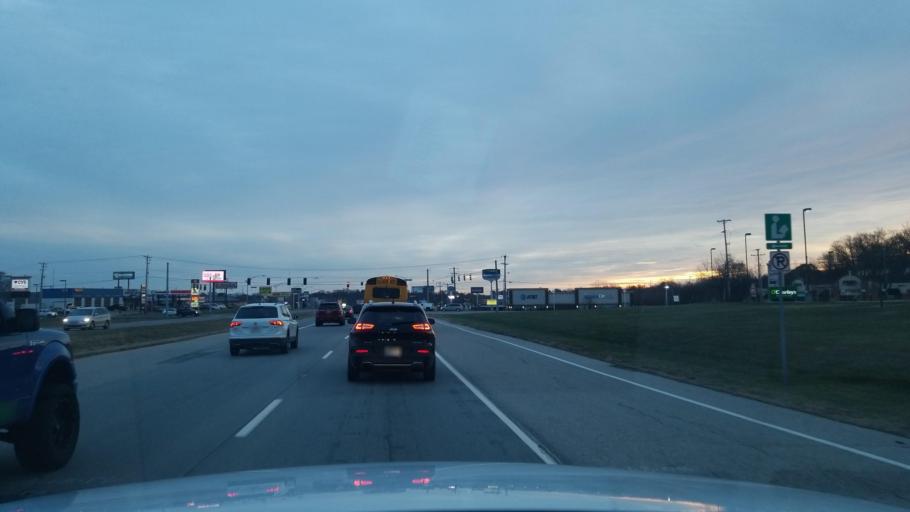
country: US
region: Indiana
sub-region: Vanderburgh County
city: Evansville
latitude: 37.9761
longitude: -87.6387
